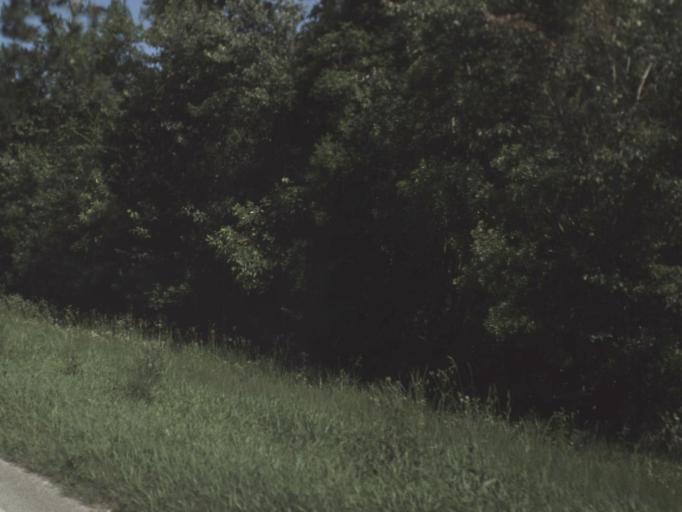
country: US
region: Florida
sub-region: Duval County
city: Baldwin
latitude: 30.3031
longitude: -81.9537
